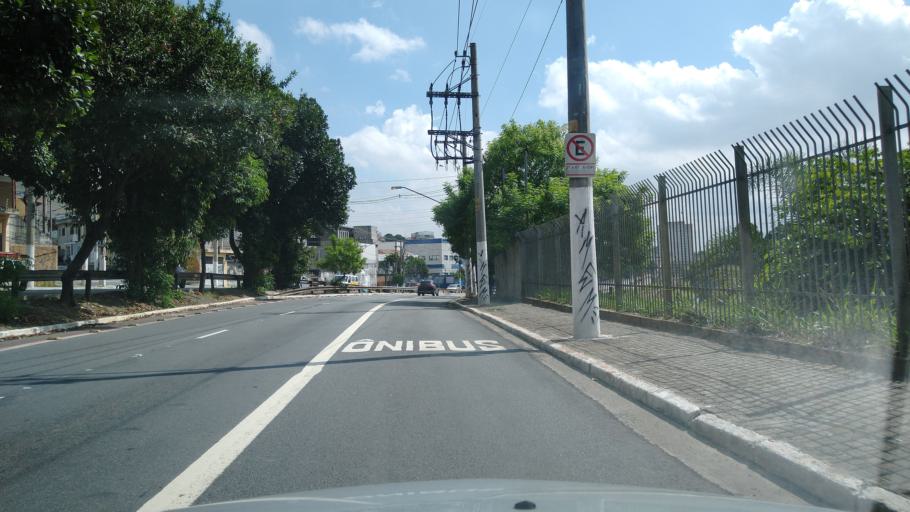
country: BR
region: Sao Paulo
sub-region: Guarulhos
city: Guarulhos
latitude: -23.4856
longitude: -46.4833
